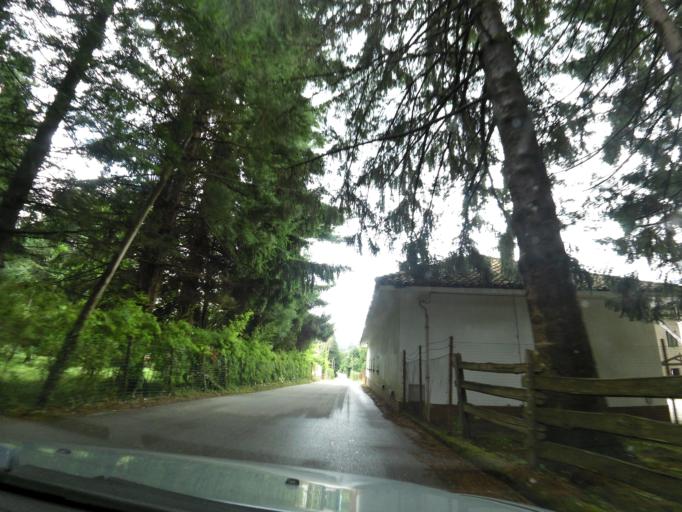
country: IT
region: Calabria
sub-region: Provincia di Vibo-Valentia
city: Serra San Bruno
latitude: 38.5611
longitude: 16.3154
